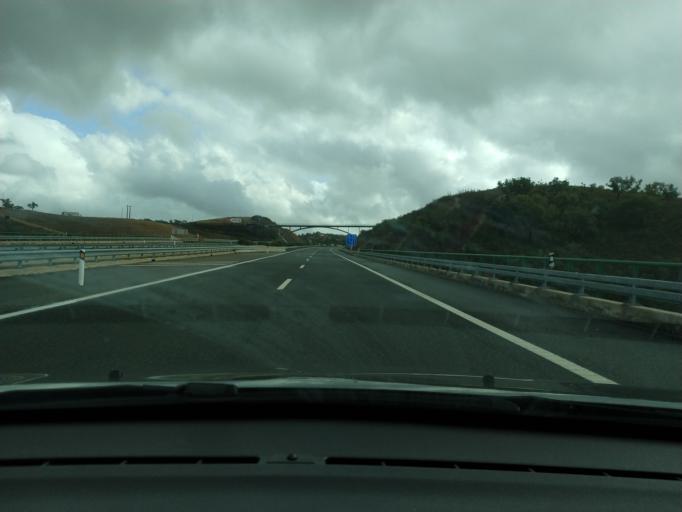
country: PT
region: Beja
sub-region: Almodovar
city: Almodovar
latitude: 37.4490
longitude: -8.2279
